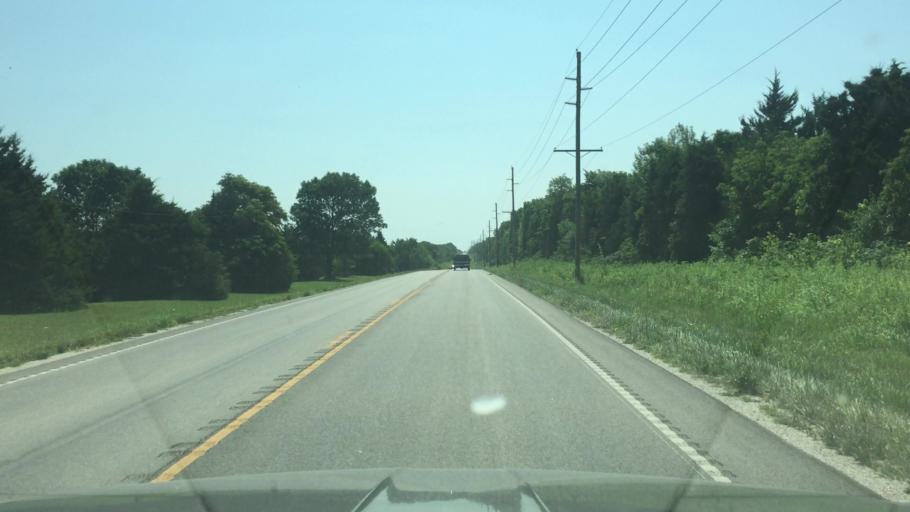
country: US
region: Missouri
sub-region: Morgan County
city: Versailles
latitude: 38.4015
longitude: -92.7454
